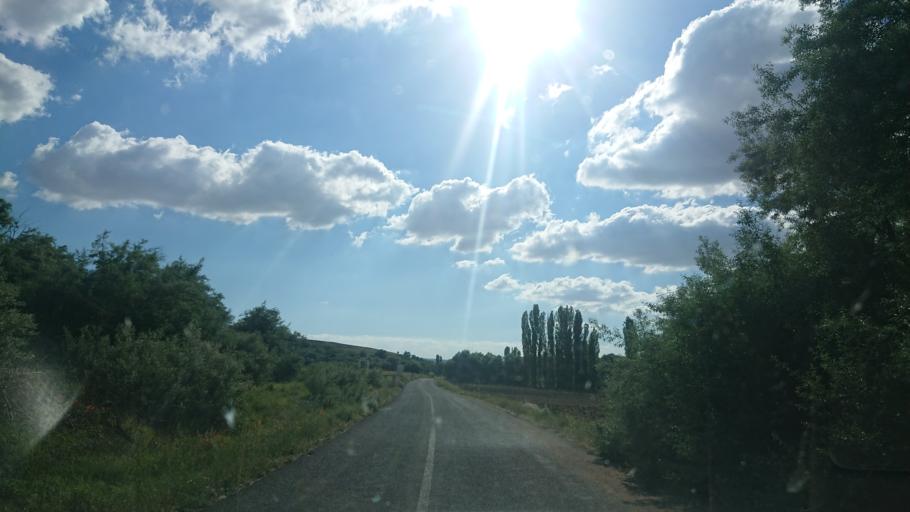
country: TR
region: Aksaray
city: Agacoren
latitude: 38.7572
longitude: 33.8901
